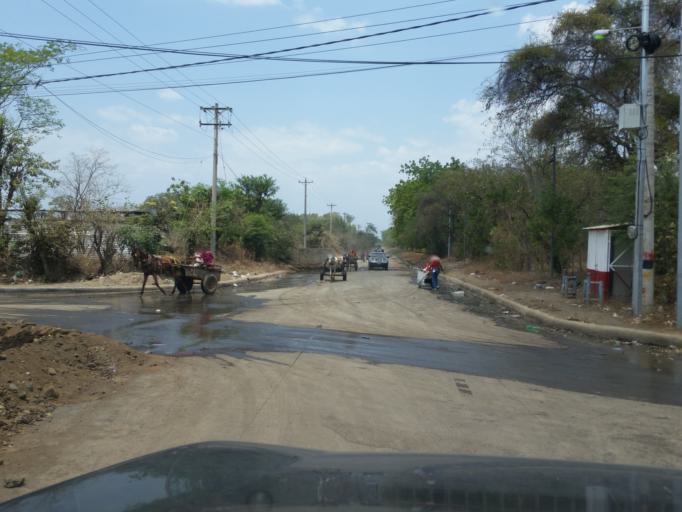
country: NI
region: Managua
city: Managua
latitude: 12.1226
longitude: -86.1656
